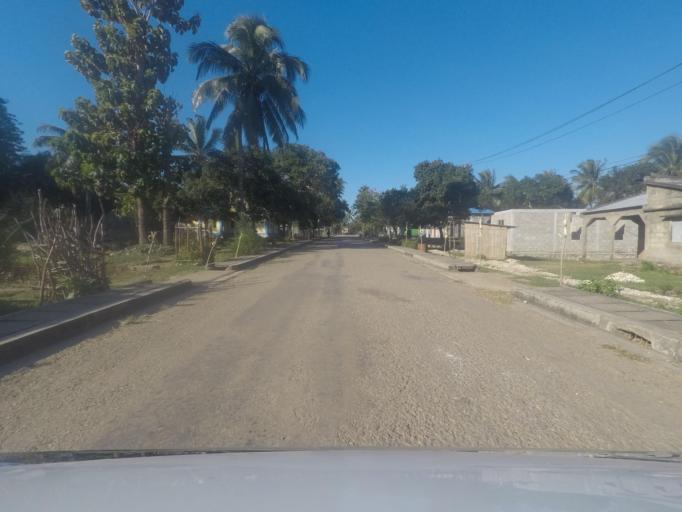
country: TL
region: Lautem
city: Lospalos
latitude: -8.4008
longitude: 127.1830
